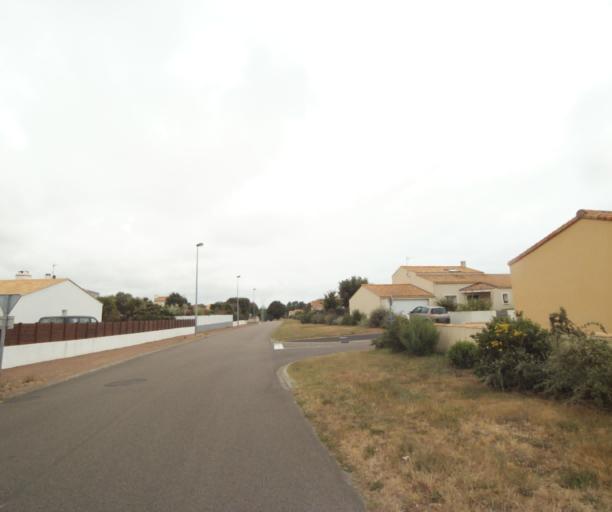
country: FR
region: Pays de la Loire
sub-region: Departement de la Vendee
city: Chateau-d'Olonne
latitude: 46.4994
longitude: -1.7455
